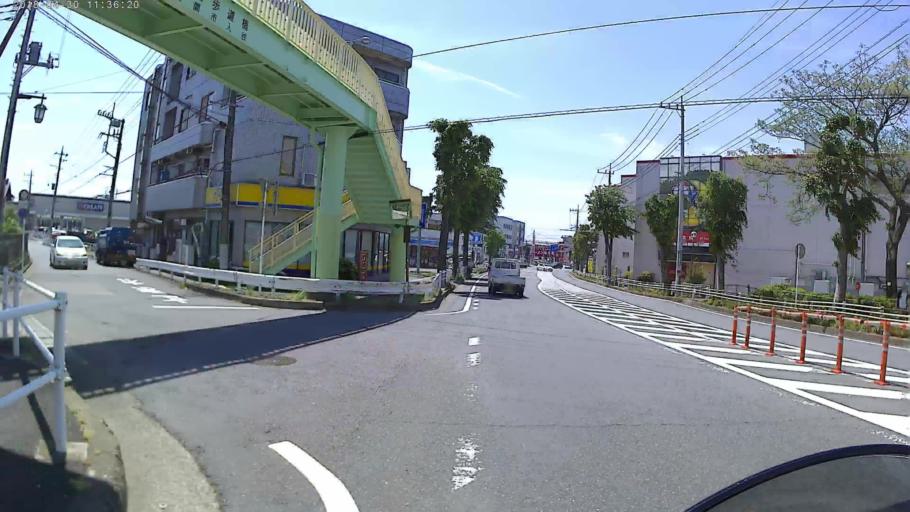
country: JP
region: Kanagawa
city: Zama
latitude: 35.4835
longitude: 139.3955
